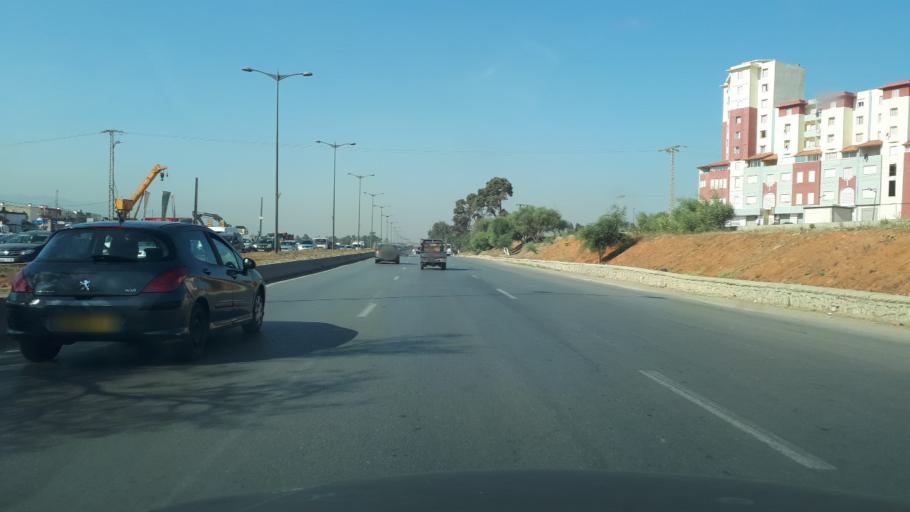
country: DZ
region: Tipaza
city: Saoula
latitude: 36.6705
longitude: 3.0467
